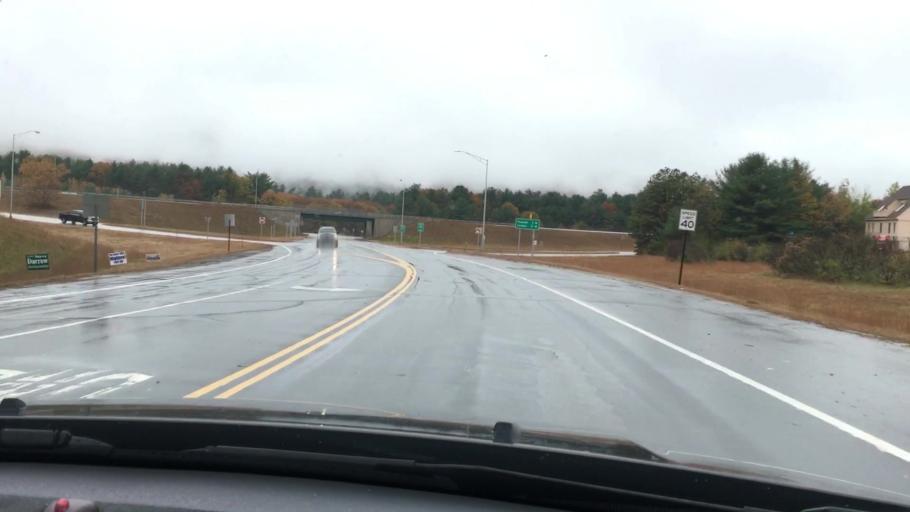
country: US
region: New Hampshire
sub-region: Grafton County
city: Ashland
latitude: 43.6985
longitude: -71.6428
